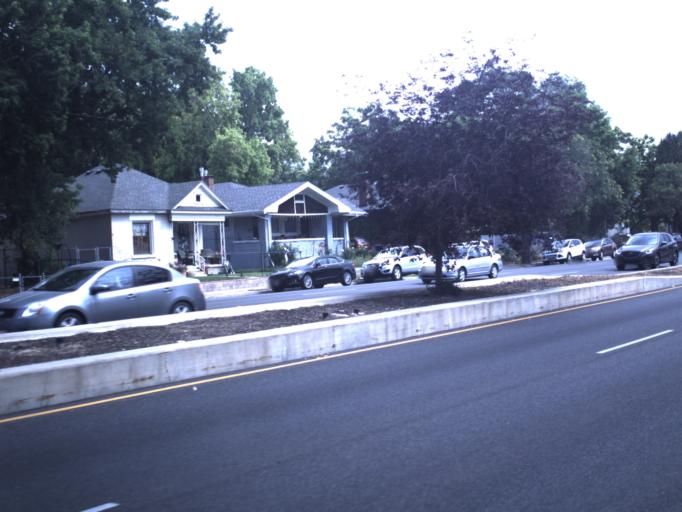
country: US
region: Utah
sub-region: Salt Lake County
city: Salt Lake City
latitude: 40.7430
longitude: -111.8713
